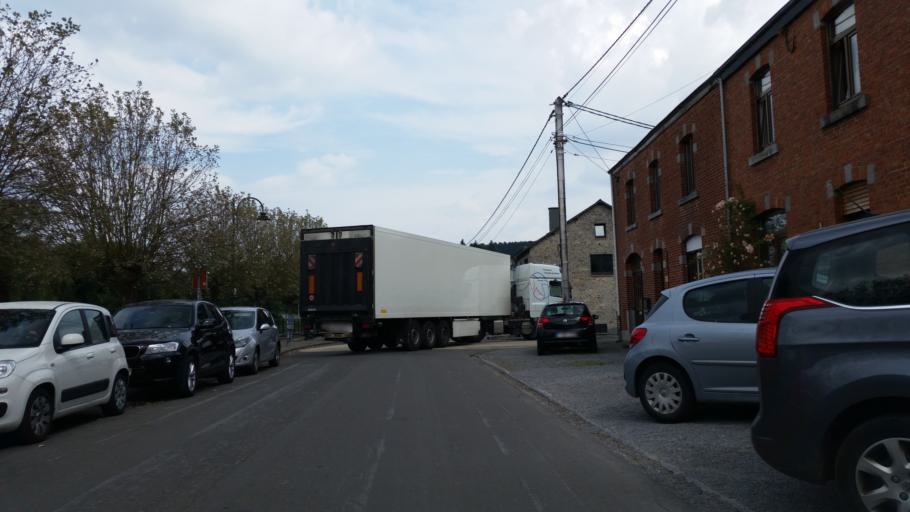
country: BE
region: Wallonia
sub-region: Province de Namur
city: Rochefort
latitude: 50.1273
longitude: 5.1857
